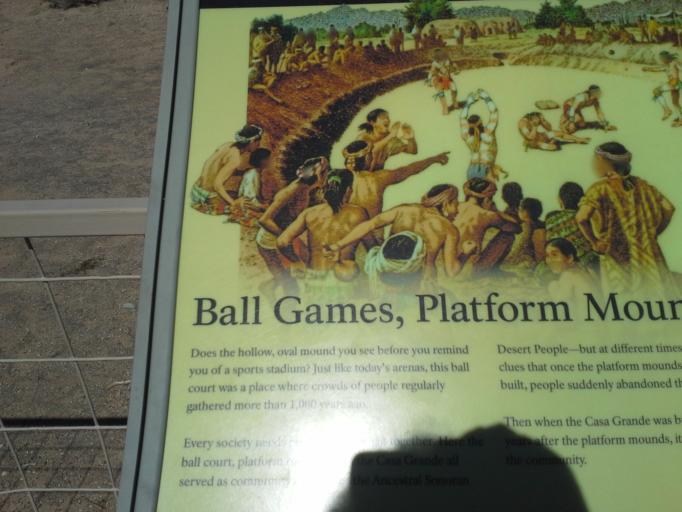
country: US
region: Arizona
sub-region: Pinal County
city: Coolidge
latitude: 32.9960
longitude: -111.5366
